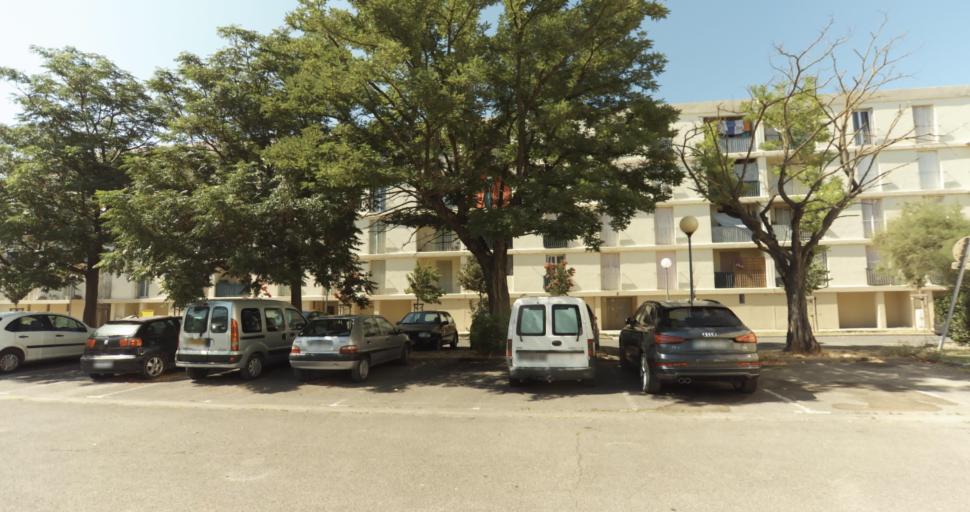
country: FR
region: Provence-Alpes-Cote d'Azur
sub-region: Departement du Vaucluse
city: Monteux
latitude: 44.0379
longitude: 5.0043
